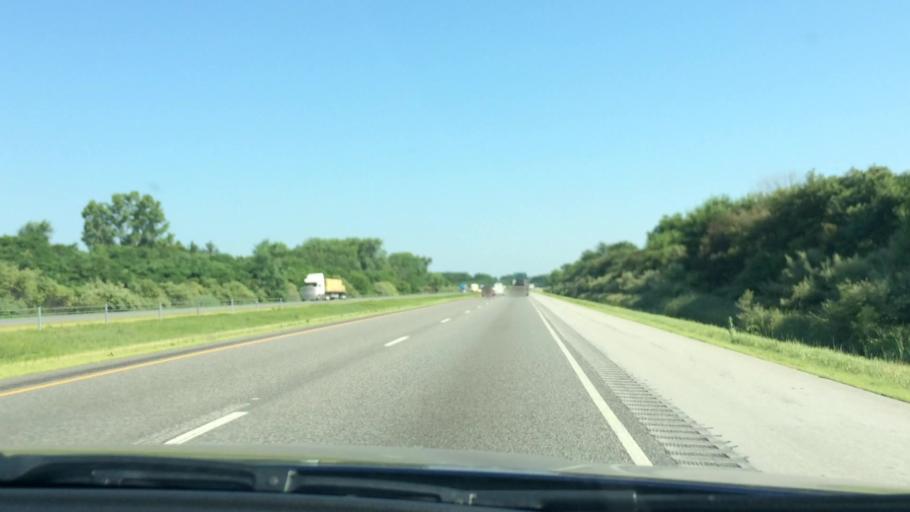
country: US
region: Indiana
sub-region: Jasper County
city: Rensselaer
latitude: 40.8673
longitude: -87.1895
